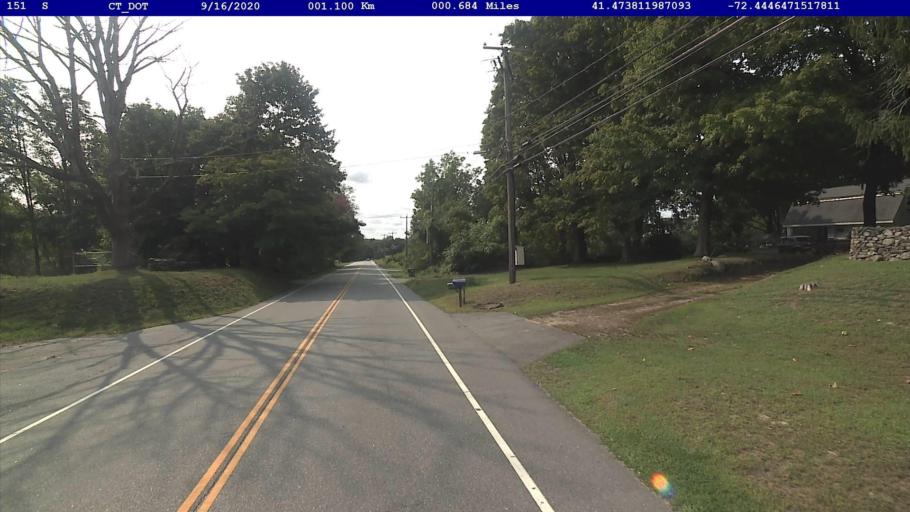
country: US
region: Connecticut
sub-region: Middlesex County
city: East Haddam
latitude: 41.4738
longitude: -72.4446
